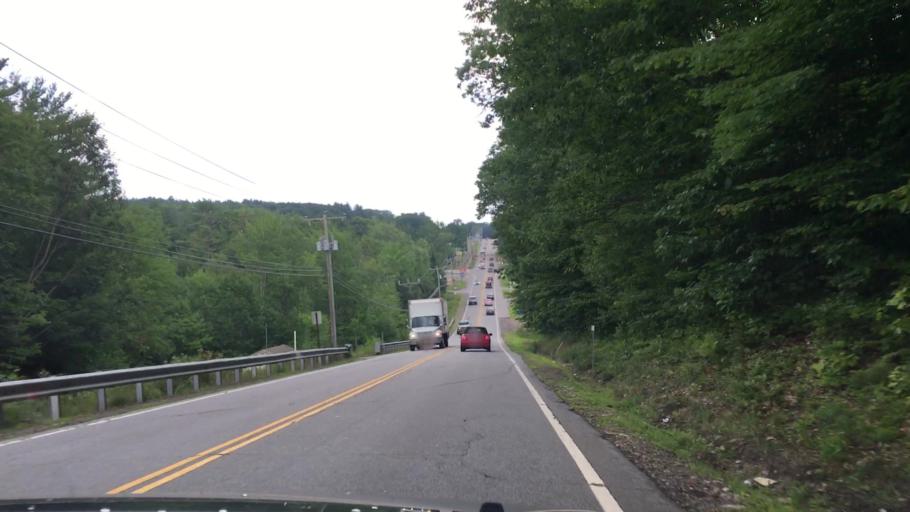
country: US
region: New Hampshire
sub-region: Belknap County
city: Meredith
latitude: 43.6203
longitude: -71.4834
